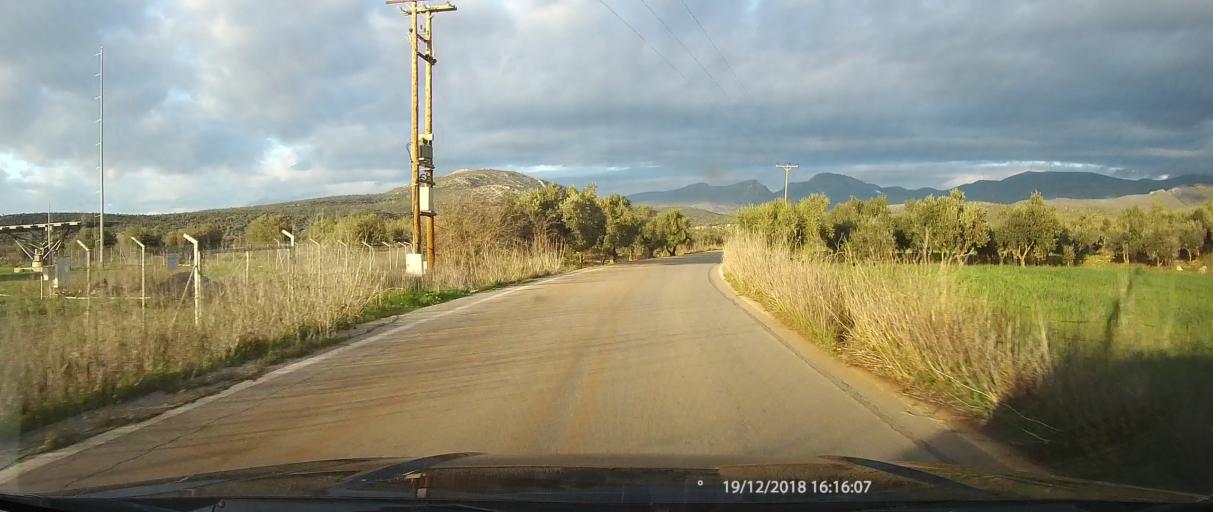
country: GR
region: Peloponnese
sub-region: Nomos Lakonias
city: Kato Glikovrisi
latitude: 36.8959
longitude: 22.8029
